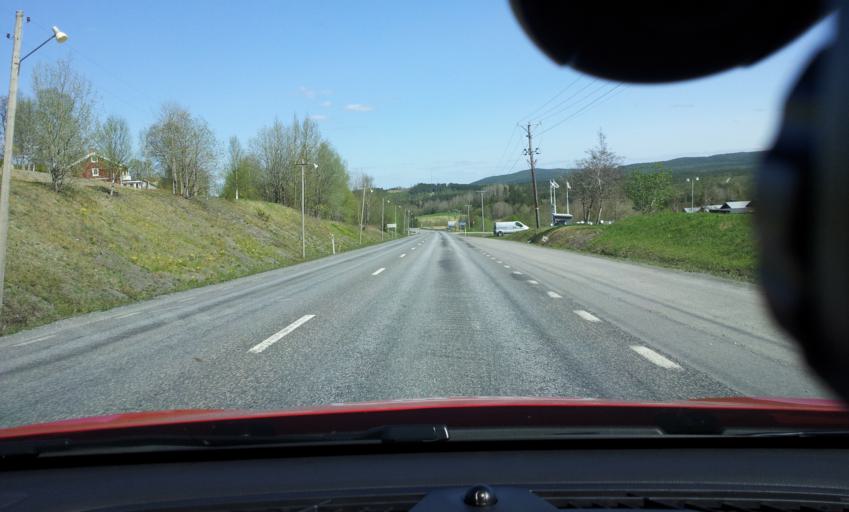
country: SE
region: Jaemtland
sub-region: Are Kommun
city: Jarpen
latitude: 63.3129
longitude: 13.3193
